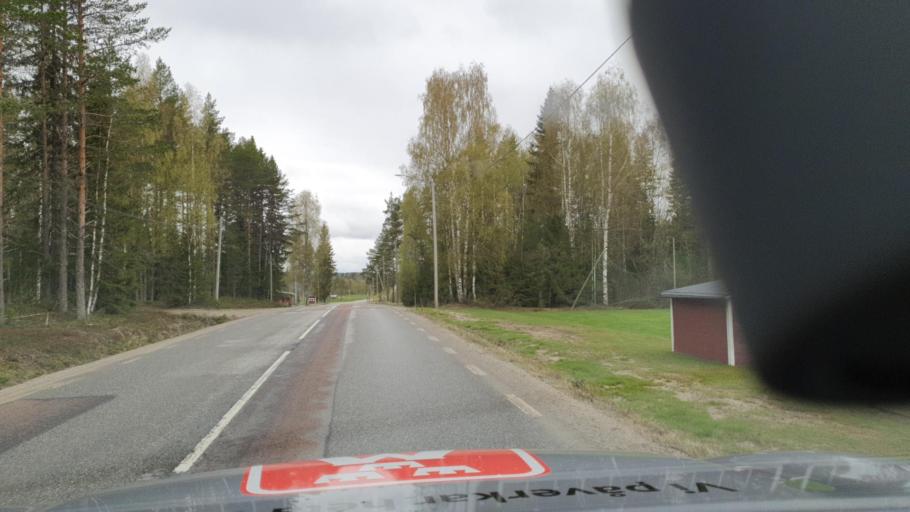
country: SE
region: Vaesternorrland
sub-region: OErnskoeldsviks Kommun
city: Bredbyn
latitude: 63.5608
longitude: 17.6499
